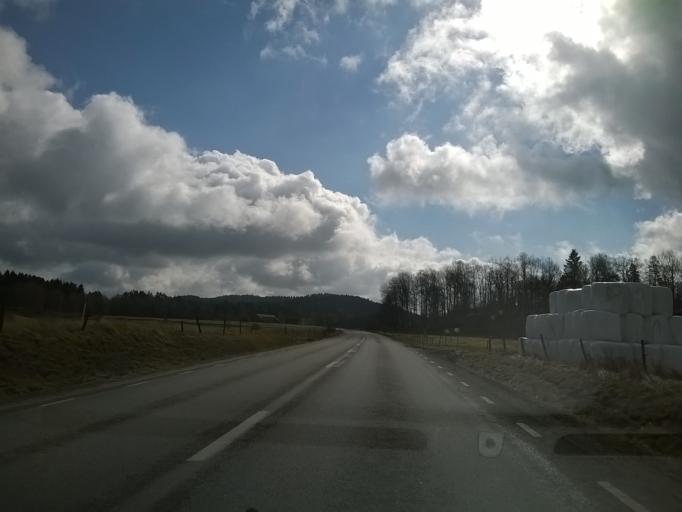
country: SE
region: Vaestra Goetaland
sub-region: Marks Kommun
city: Horred
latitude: 57.1505
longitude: 12.6808
